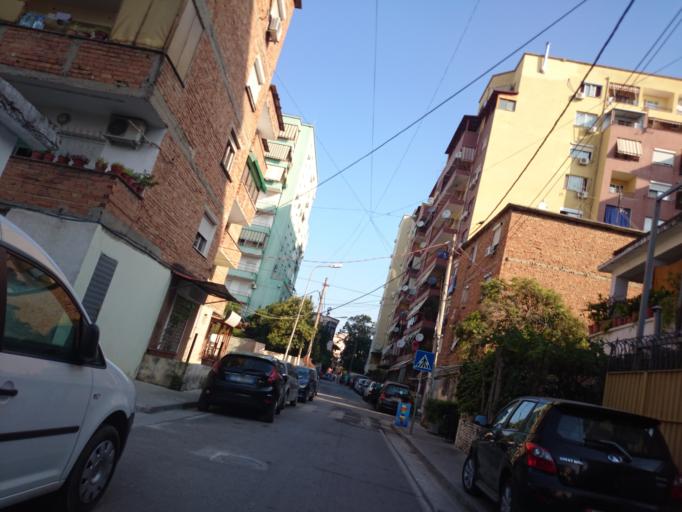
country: AL
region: Tirane
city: Tirana
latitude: 41.3259
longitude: 19.8099
